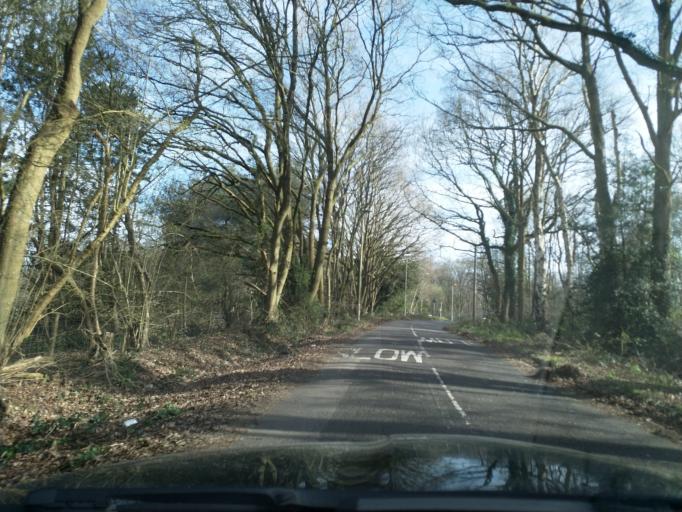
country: GB
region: England
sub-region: Hampshire
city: Farnborough
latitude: 51.2830
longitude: -0.7911
